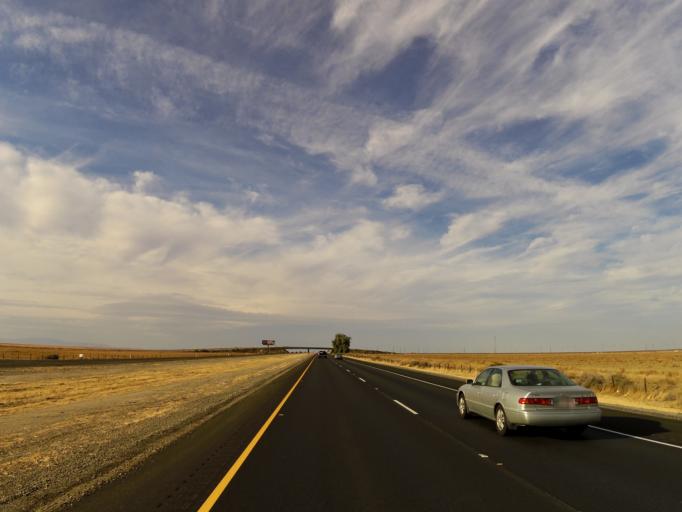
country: US
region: California
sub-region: Kern County
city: Lost Hills
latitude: 35.6610
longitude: -119.6863
